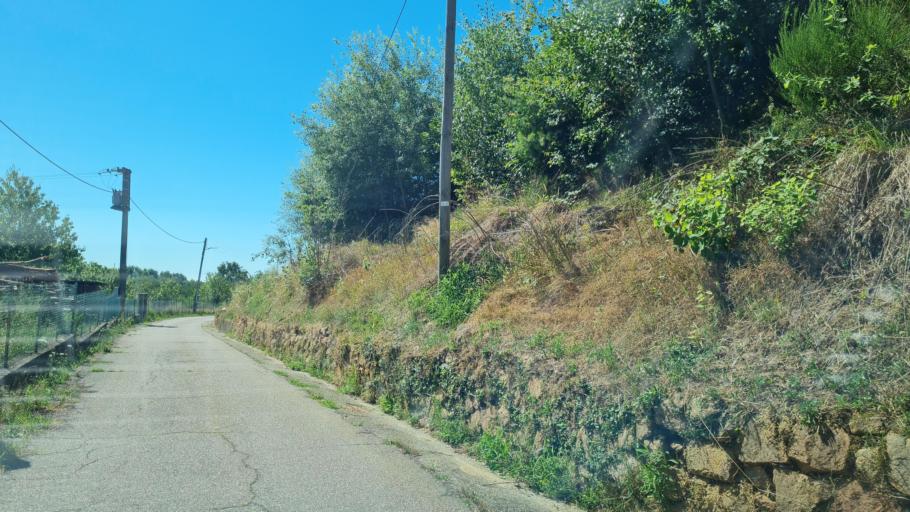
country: IT
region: Piedmont
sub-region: Provincia di Biella
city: Masserano
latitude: 45.5889
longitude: 8.2194
